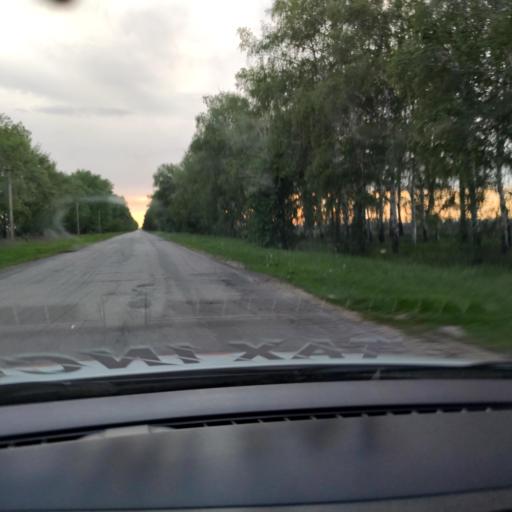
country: RU
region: Voronezj
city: Maslovka
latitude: 51.4386
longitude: 39.2925
